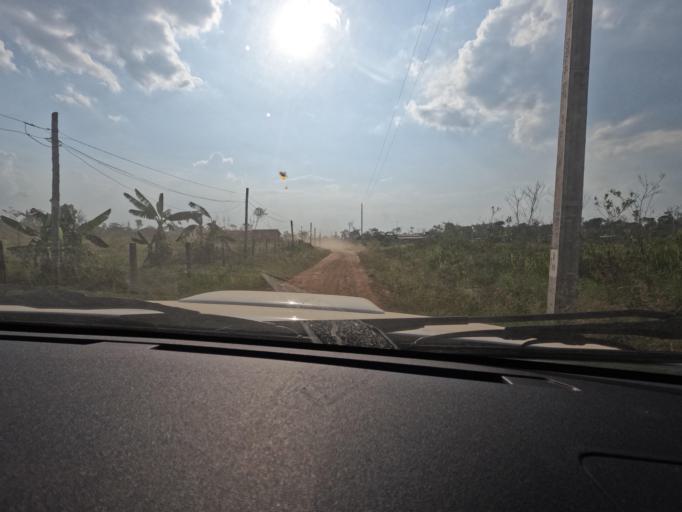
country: BR
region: Rondonia
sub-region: Porto Velho
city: Porto Velho
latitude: -8.5747
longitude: -63.9976
